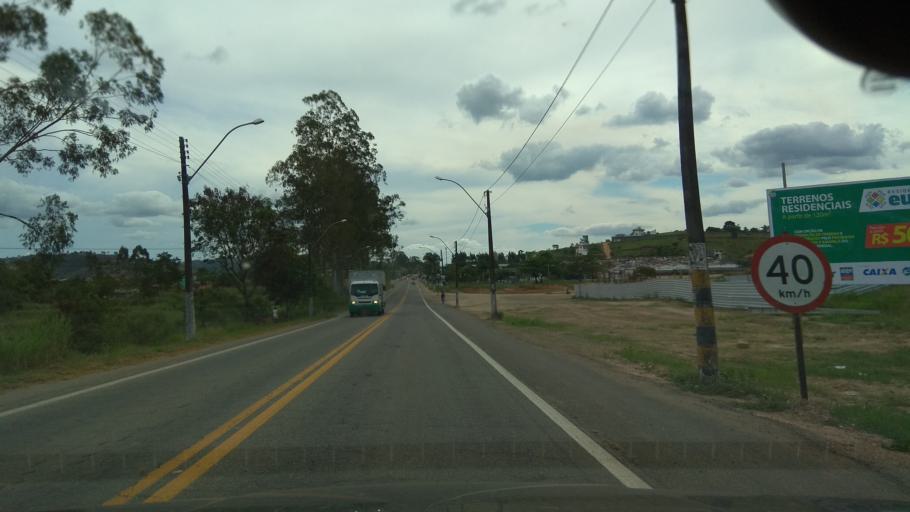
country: BR
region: Bahia
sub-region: Ipiau
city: Ipiau
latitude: -14.1427
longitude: -39.7210
